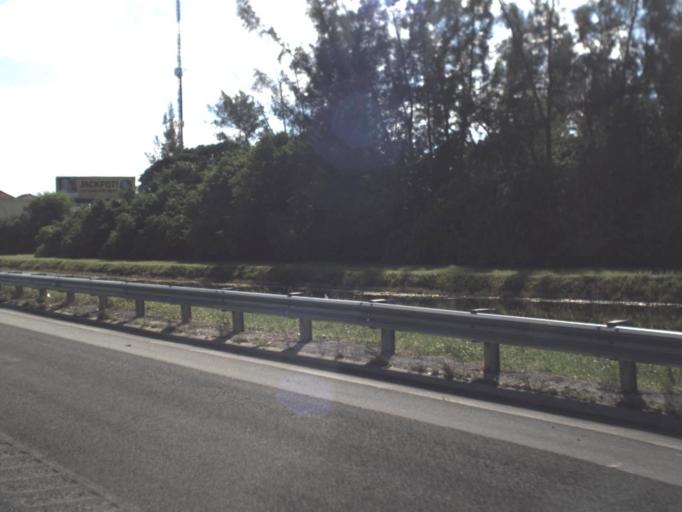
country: US
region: Florida
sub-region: Palm Beach County
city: Boca Del Mar
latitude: 26.3730
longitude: -80.1710
